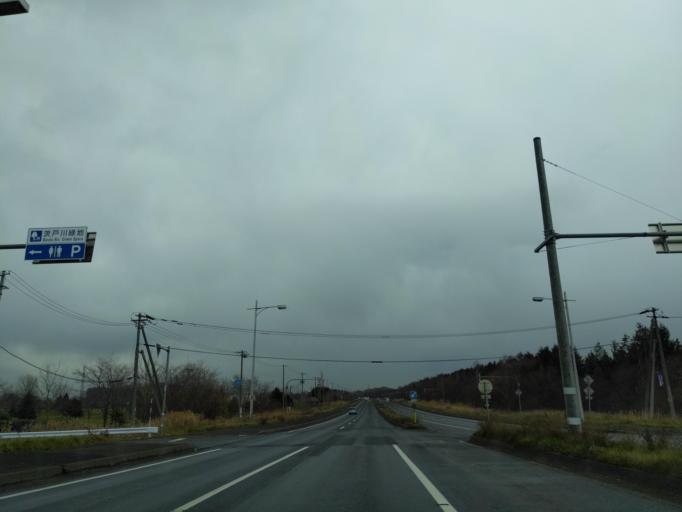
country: JP
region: Hokkaido
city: Ishikari
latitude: 43.1737
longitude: 141.3916
